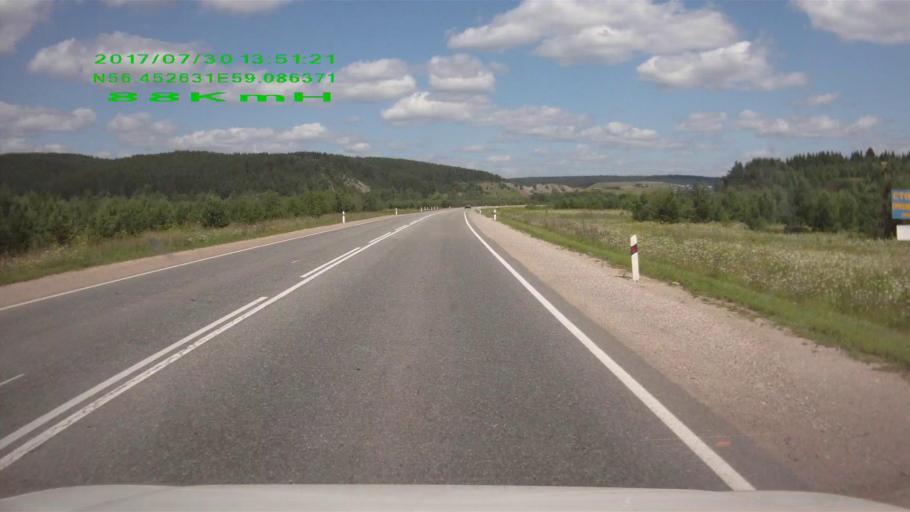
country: RU
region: Sverdlovsk
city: Mikhaylovsk
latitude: 56.4530
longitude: 59.0868
